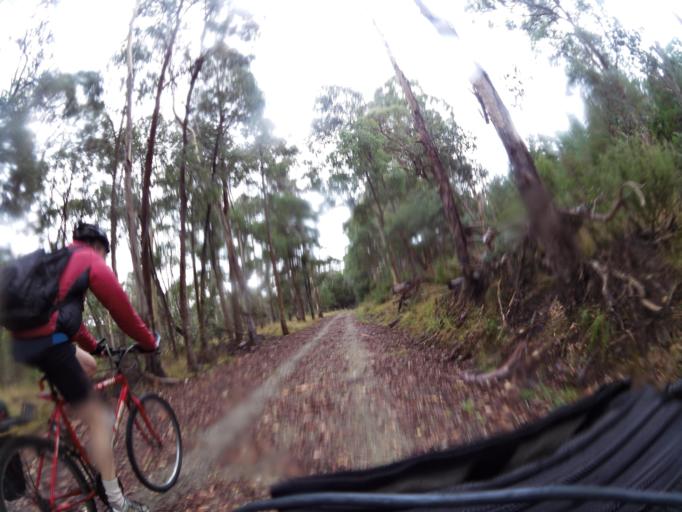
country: AU
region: New South Wales
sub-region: Greater Hume Shire
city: Holbrook
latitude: -36.1787
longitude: 147.5008
